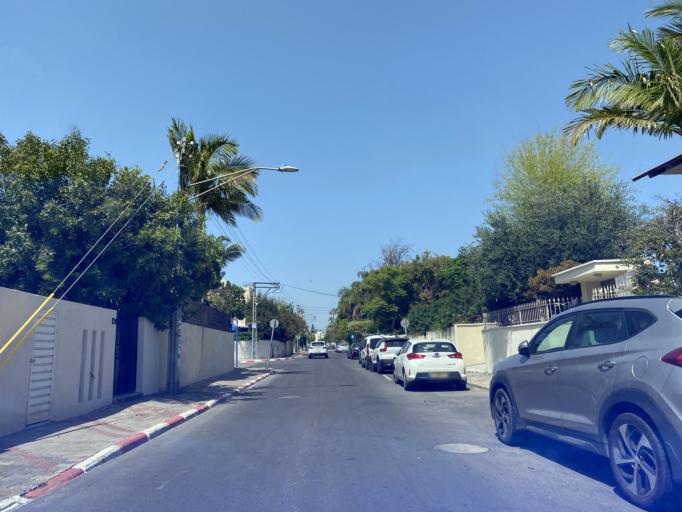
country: IL
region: Tel Aviv
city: Herzliya Pituah
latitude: 32.1703
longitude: 34.8095
